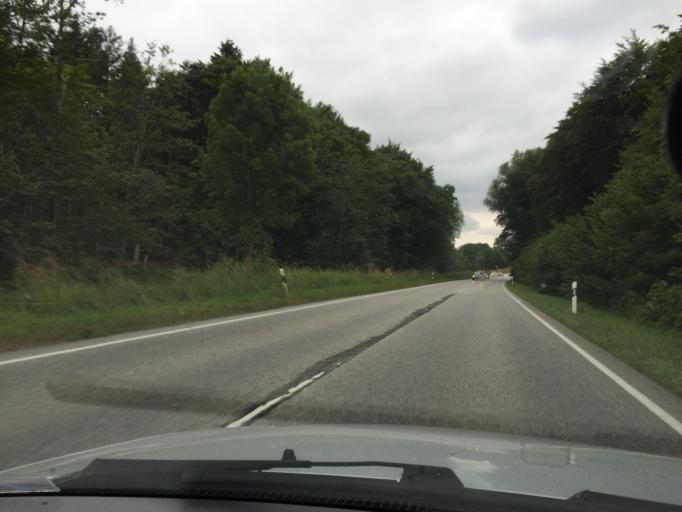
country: DE
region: Schleswig-Holstein
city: Oeversee
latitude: 54.6756
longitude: 9.4383
